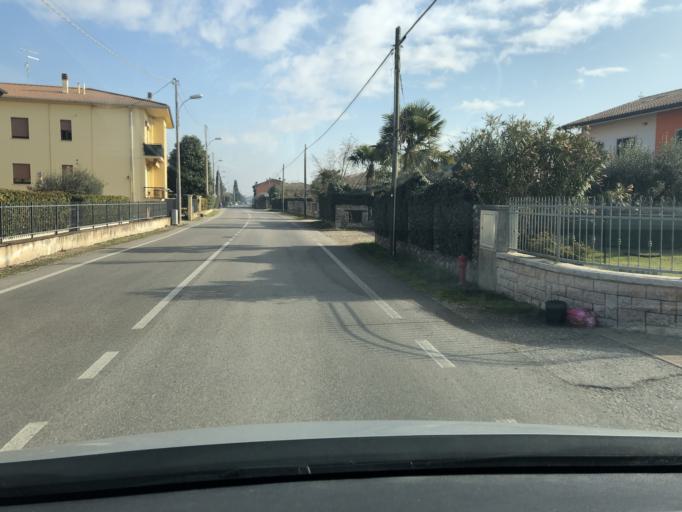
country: IT
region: Veneto
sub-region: Provincia di Verona
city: Sona
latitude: 45.4321
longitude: 10.8579
